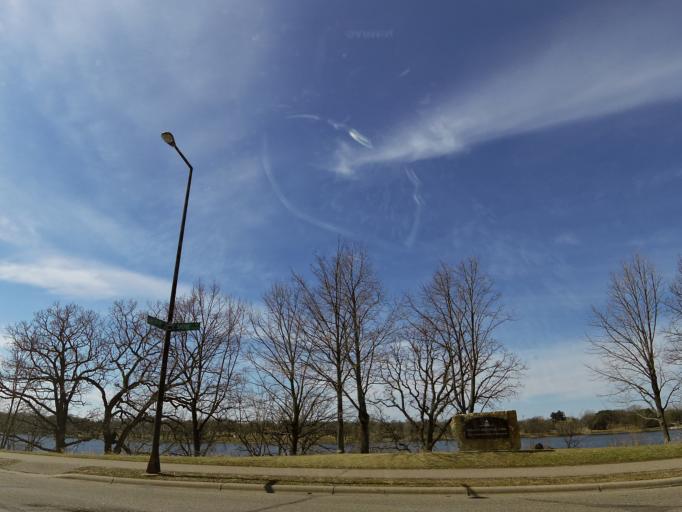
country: US
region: Minnesota
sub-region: Ramsey County
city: Little Canada
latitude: 44.9921
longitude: -93.0520
